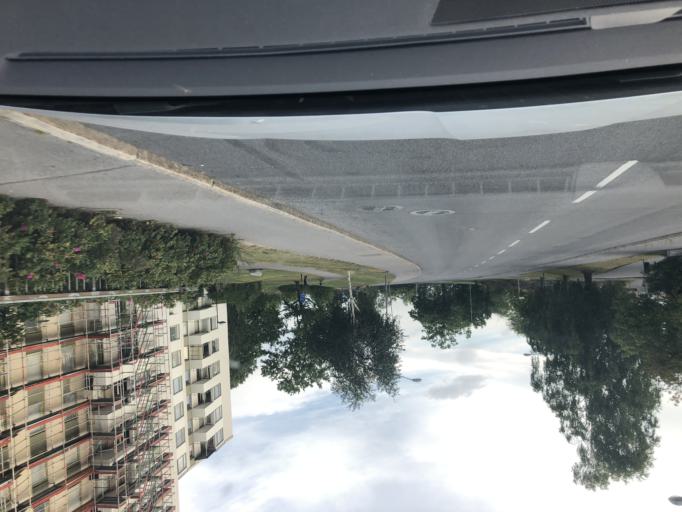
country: SE
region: Stockholm
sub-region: Botkyrka Kommun
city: Fittja
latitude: 59.2768
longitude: 17.8864
